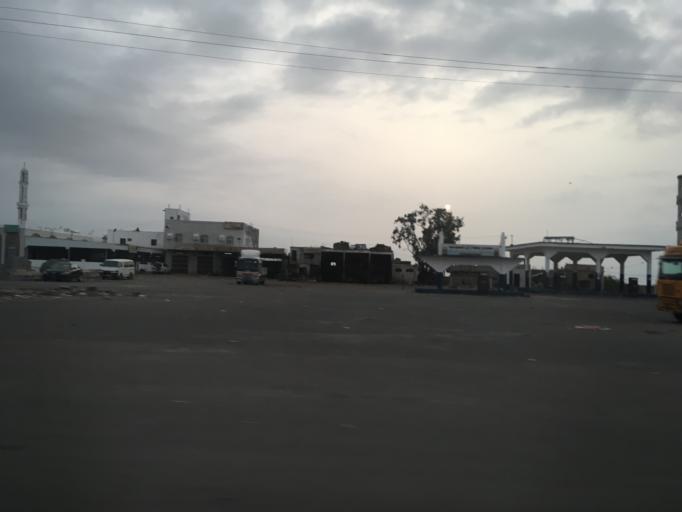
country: YE
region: Lahij
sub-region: Al  Hawtah
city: Lahij
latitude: 13.0233
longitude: 44.8919
